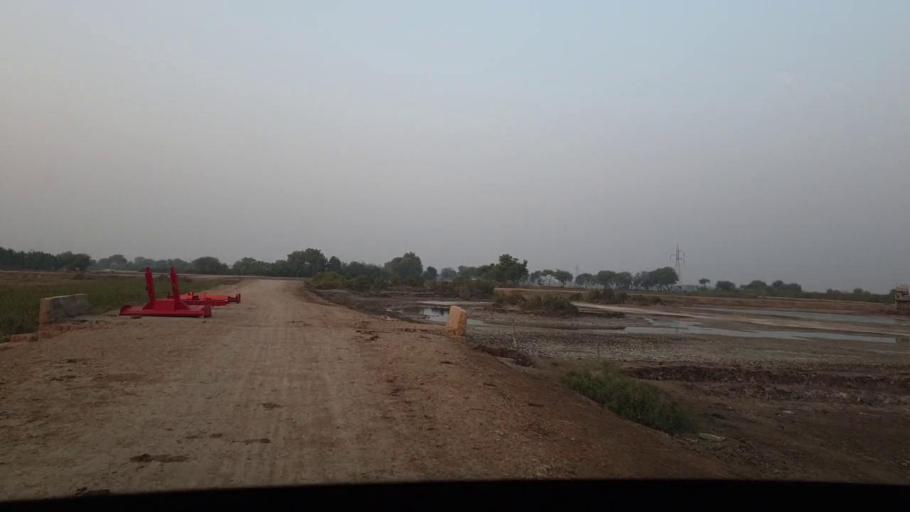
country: PK
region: Sindh
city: Chuhar Jamali
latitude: 24.4625
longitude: 68.0324
